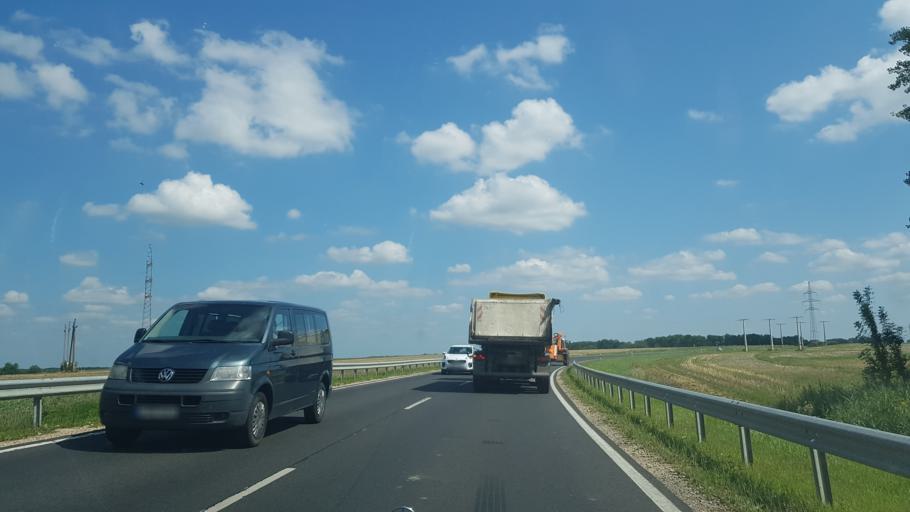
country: HU
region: Somogy
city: Marcali
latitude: 46.6064
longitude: 17.4160
